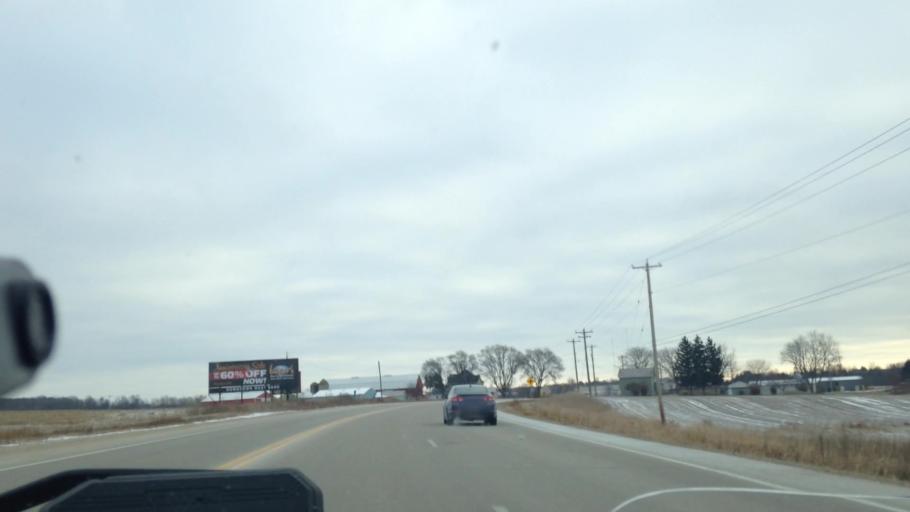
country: US
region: Wisconsin
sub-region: Washington County
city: Slinger
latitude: 43.4271
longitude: -88.3272
